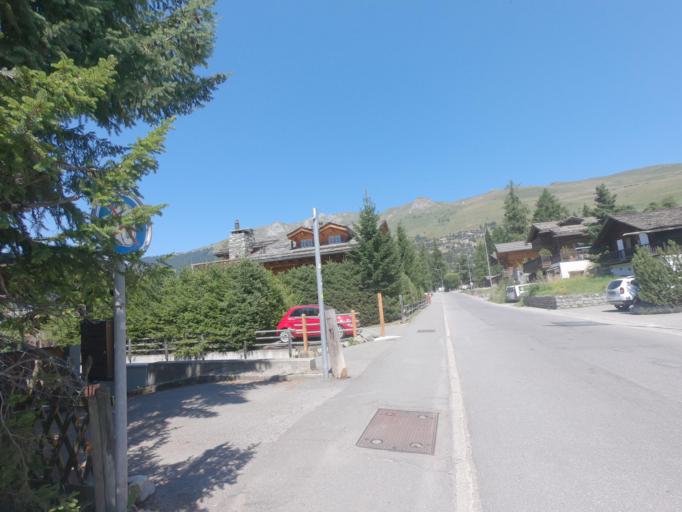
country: CH
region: Valais
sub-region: Entremont District
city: Verbier
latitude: 46.0986
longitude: 7.2321
